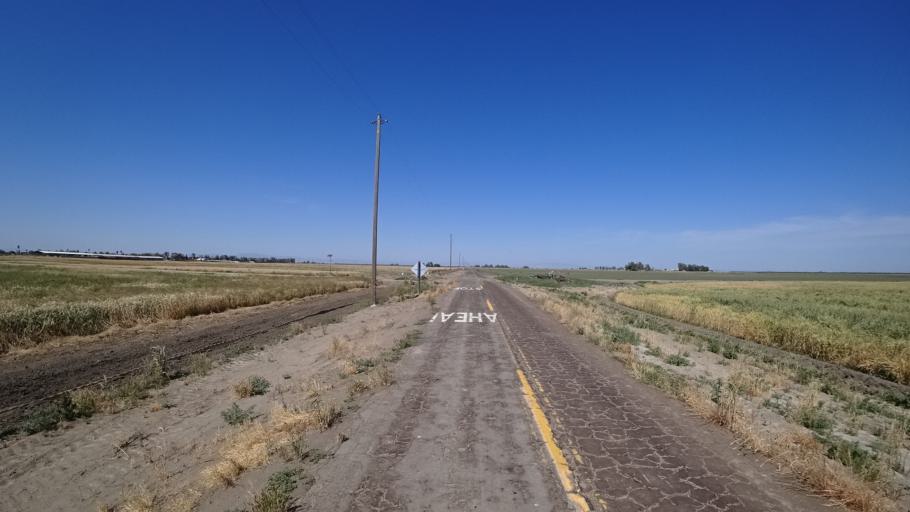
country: US
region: California
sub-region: Kings County
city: Stratford
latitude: 36.1968
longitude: -119.8246
